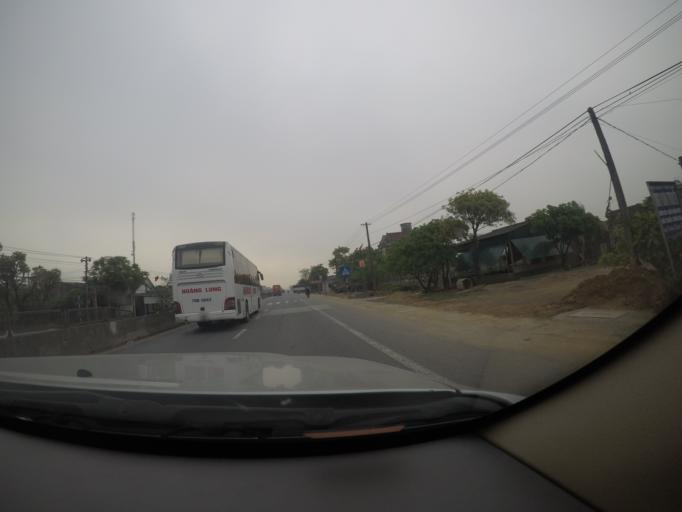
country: VN
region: Ha Tinh
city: Cam Xuyen
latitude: 18.2157
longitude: 106.0948
